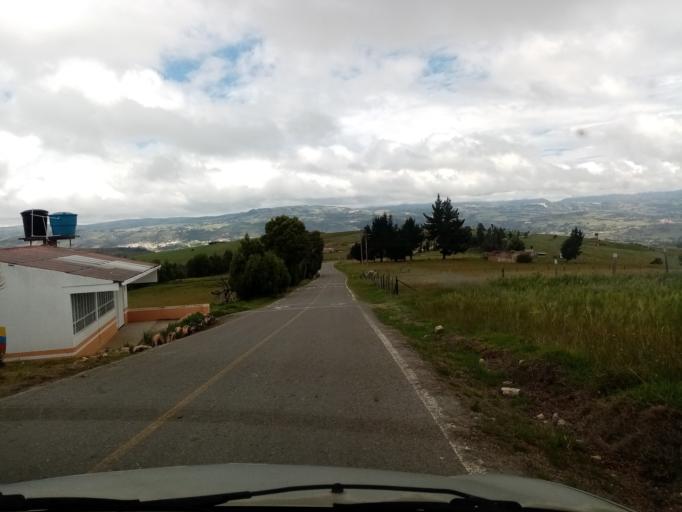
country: CO
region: Boyaca
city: Siachoque
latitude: 5.5650
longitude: -73.2900
